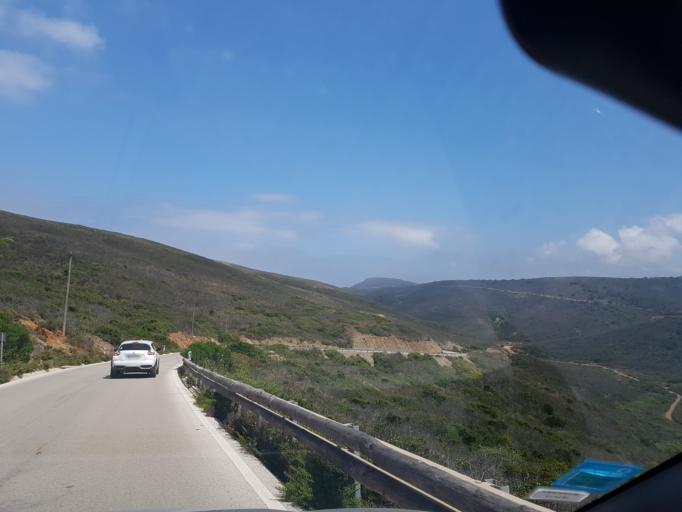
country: PT
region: Faro
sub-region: Vila do Bispo
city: Vila do Bispo
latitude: 37.0999
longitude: -8.9367
